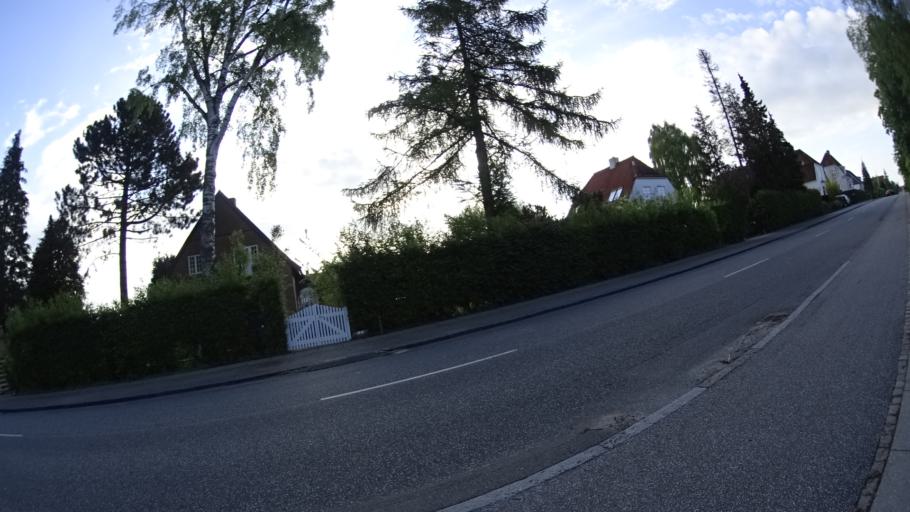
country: DK
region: Central Jutland
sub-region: Arhus Kommune
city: Arhus
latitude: 56.1339
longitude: 10.1795
